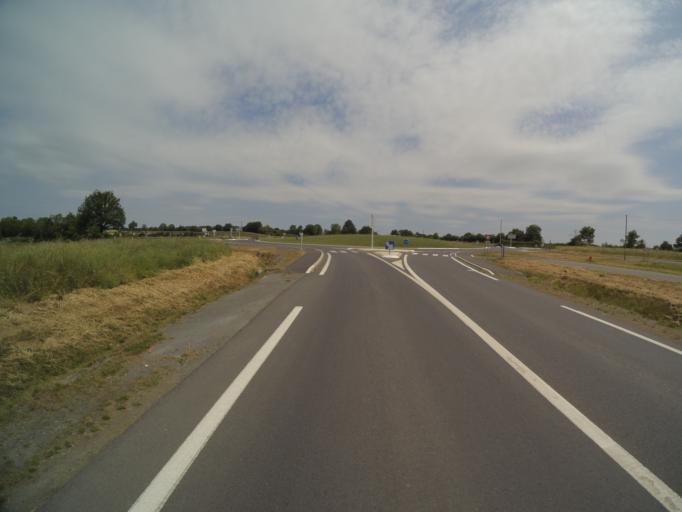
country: FR
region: Pays de la Loire
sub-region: Departement de la Vendee
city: Saint-Paul-en-Pareds
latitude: 46.8621
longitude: -0.9726
